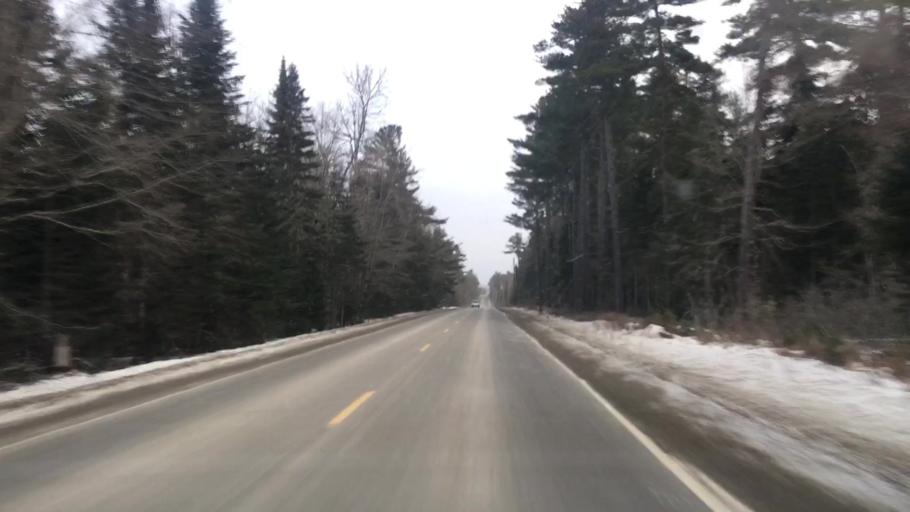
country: US
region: Maine
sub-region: Hancock County
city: Ellsworth
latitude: 44.6733
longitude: -68.3539
